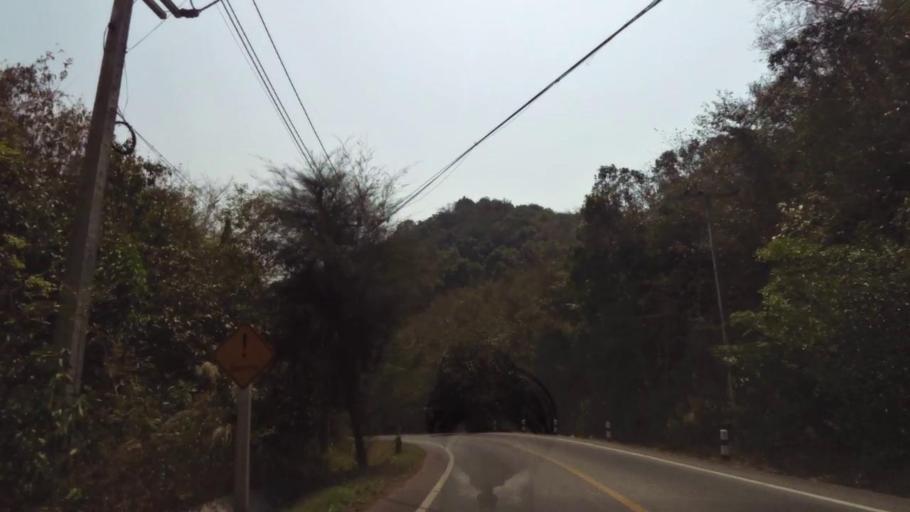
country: TH
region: Chanthaburi
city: Tha Mai
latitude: 12.5251
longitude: 101.9475
